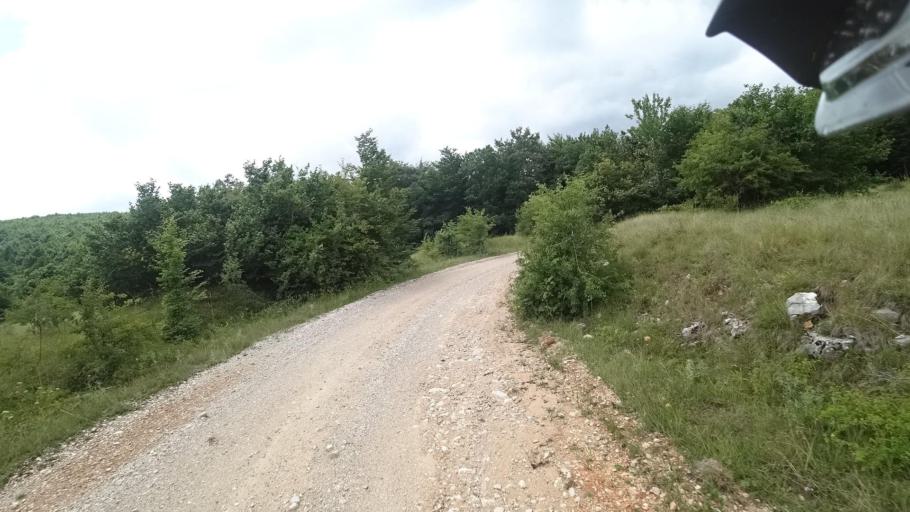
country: BA
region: Federation of Bosnia and Herzegovina
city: Bihac
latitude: 44.6650
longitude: 15.7477
